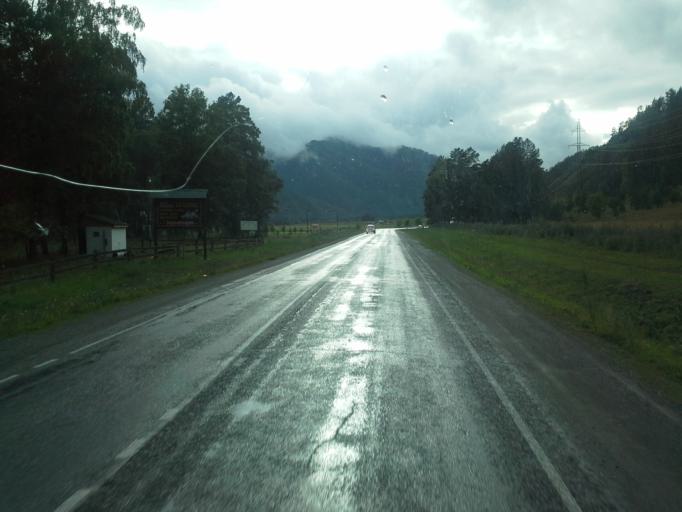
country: RU
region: Altay
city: Elekmonar
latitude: 51.5695
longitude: 85.8926
